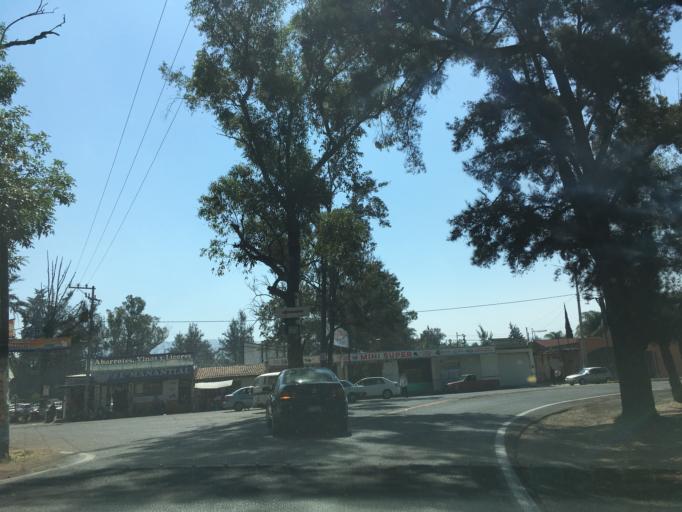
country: MX
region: Michoacan
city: Zinapecuaro
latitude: 19.8657
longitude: -100.8396
